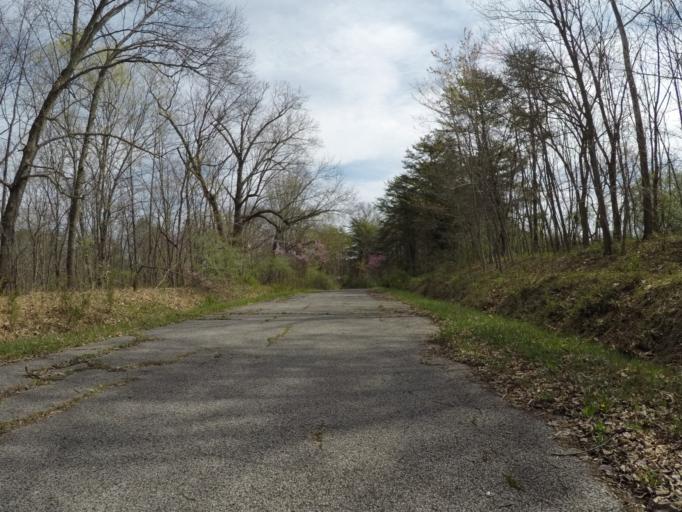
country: US
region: West Virginia
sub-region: Wayne County
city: Lavalette
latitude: 38.3209
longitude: -82.3501
